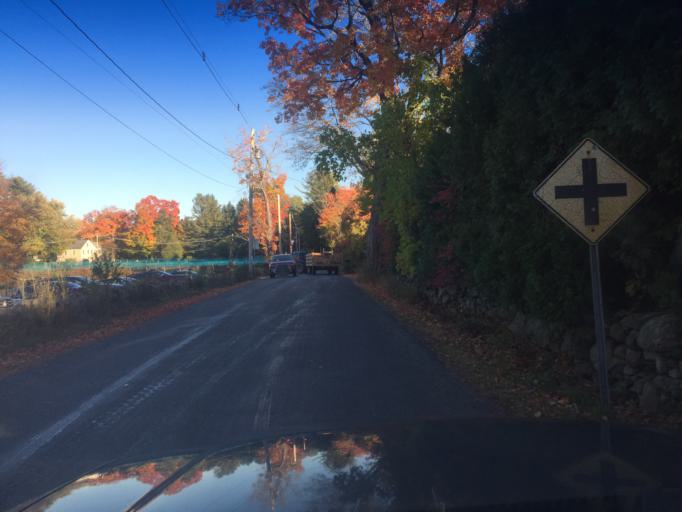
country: US
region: Massachusetts
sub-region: Middlesex County
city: Stow
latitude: 42.4120
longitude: -71.5152
